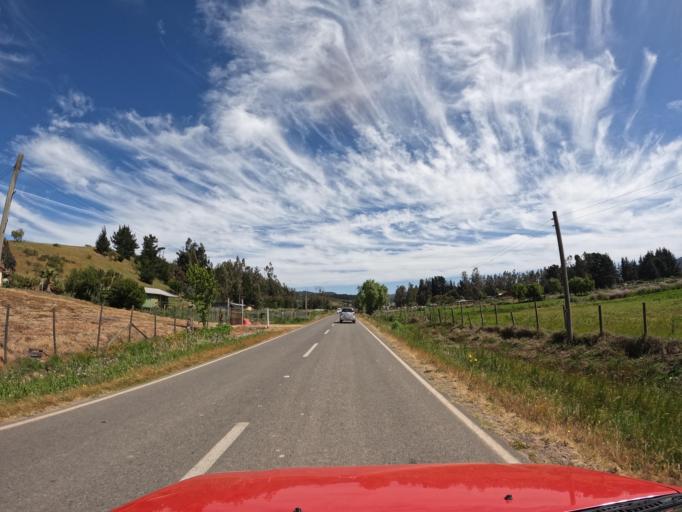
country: CL
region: Maule
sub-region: Provincia de Talca
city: Constitucion
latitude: -35.0138
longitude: -72.0373
